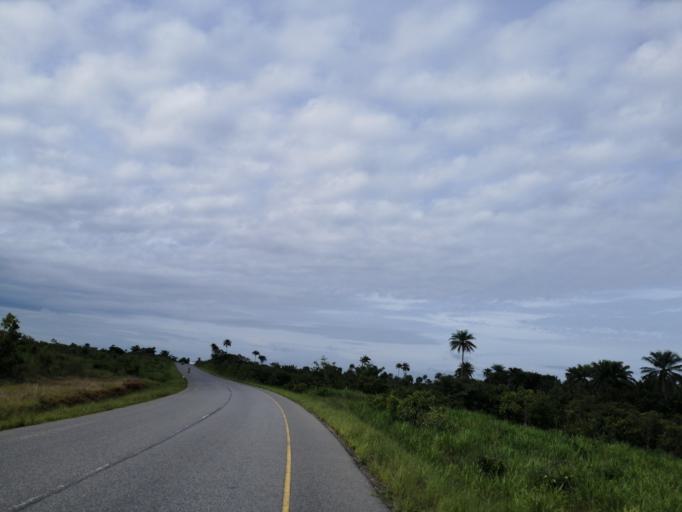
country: SL
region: Northern Province
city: Port Loko
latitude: 8.7800
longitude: -12.8571
